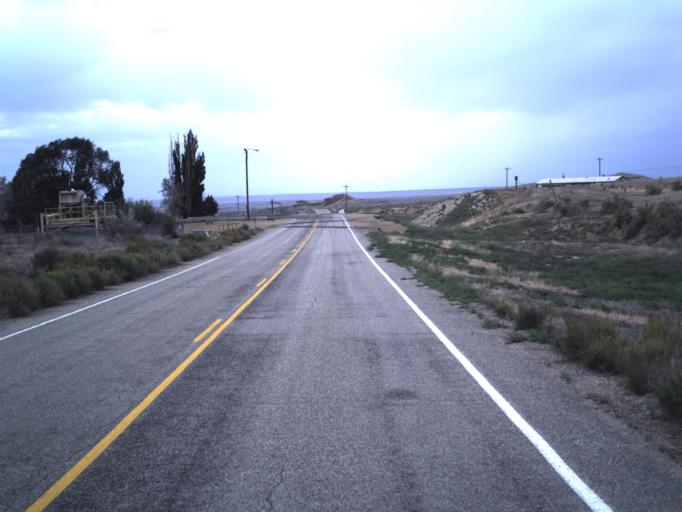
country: US
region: Colorado
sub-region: Rio Blanco County
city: Rangely
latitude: 40.0177
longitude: -109.1724
